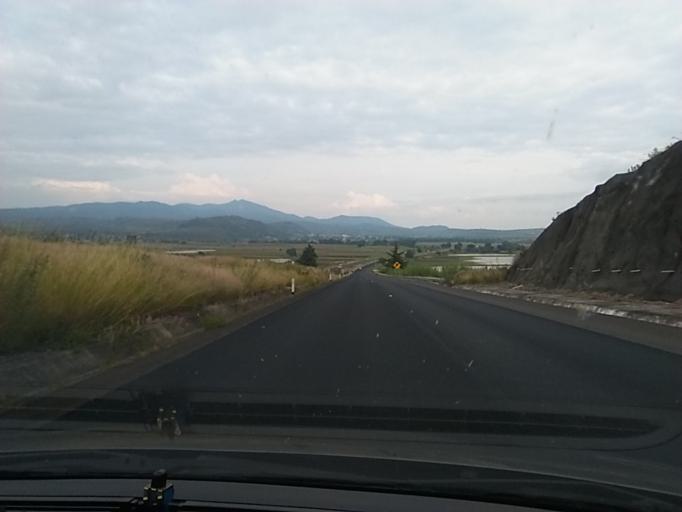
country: MX
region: Mexico
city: Huaniqueo de Morales
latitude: 19.8932
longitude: -101.5488
